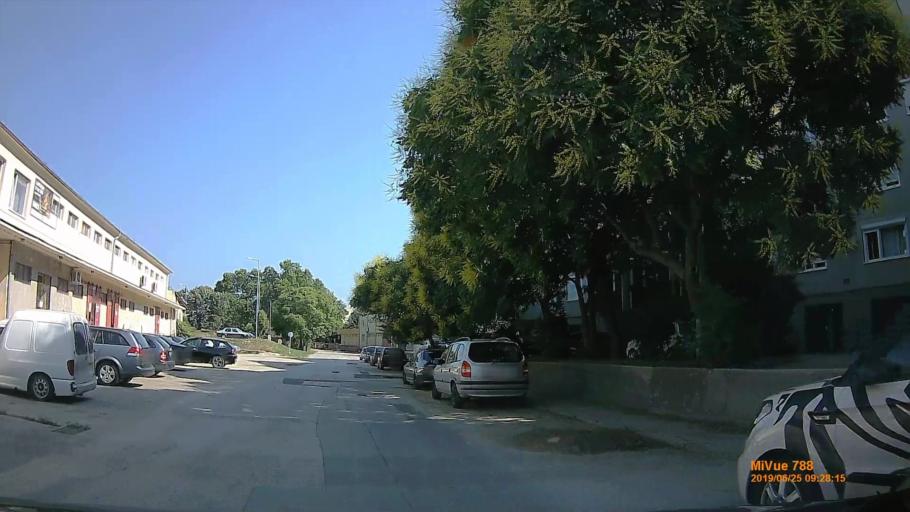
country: HU
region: Komarom-Esztergom
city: Esztergom
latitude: 47.7765
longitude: 18.7443
